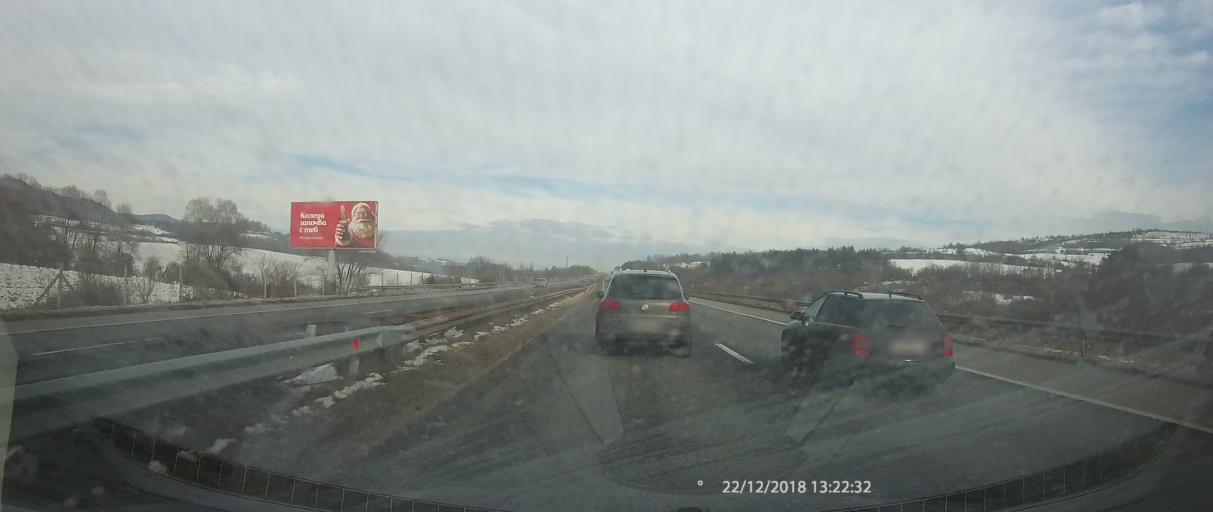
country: BG
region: Lovech
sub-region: Obshtina Yablanitsa
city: Yablanitsa
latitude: 42.9874
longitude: 24.0679
